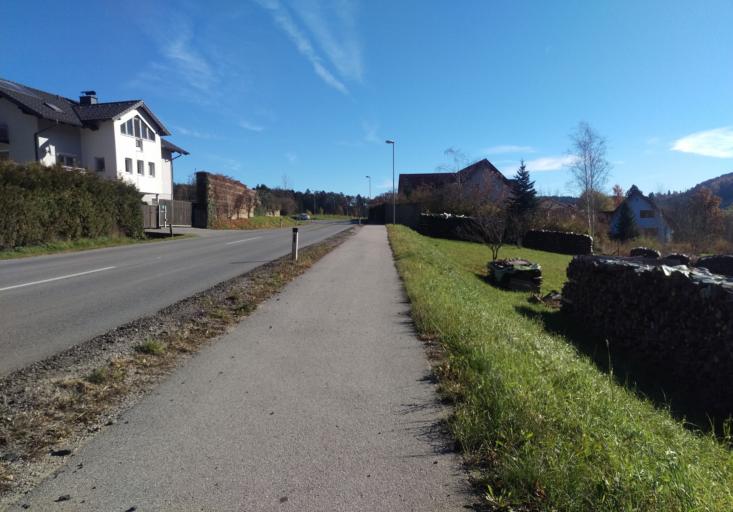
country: AT
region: Styria
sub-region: Politischer Bezirk Graz-Umgebung
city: Sankt Radegund bei Graz
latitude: 47.1382
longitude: 15.4796
